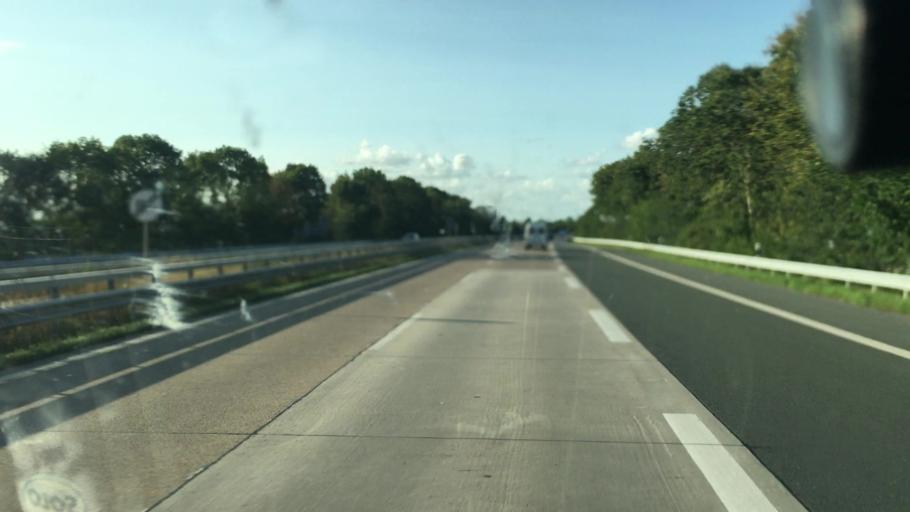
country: DE
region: Lower Saxony
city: Bockhorn
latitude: 53.4480
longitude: 8.0251
